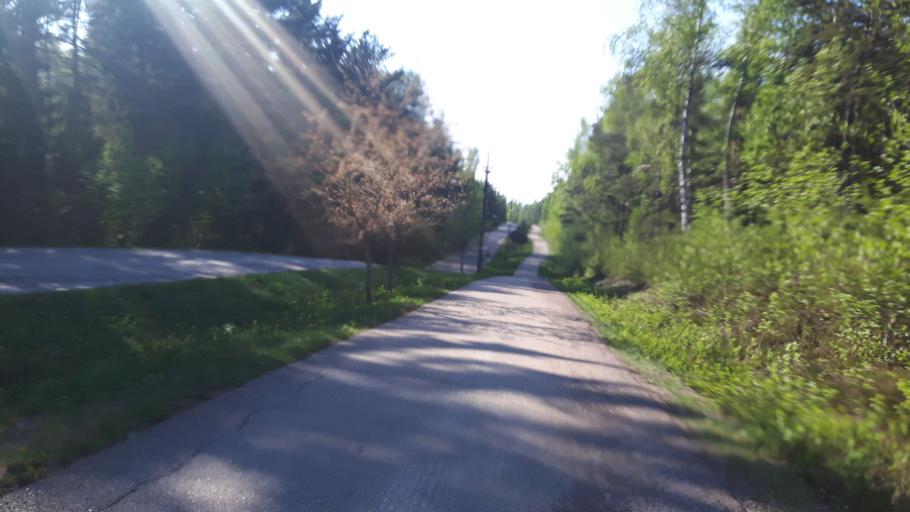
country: FI
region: Kymenlaakso
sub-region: Kotka-Hamina
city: Kotka
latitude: 60.4364
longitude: 26.8762
